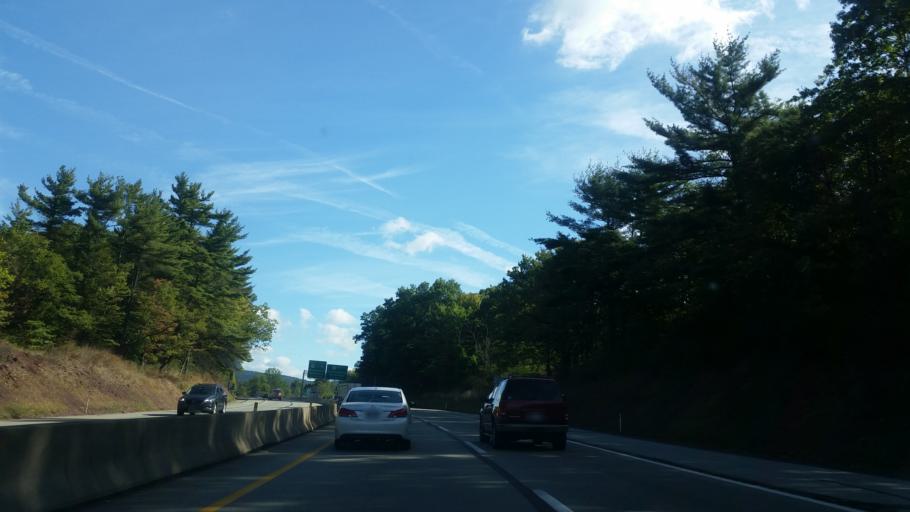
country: US
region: Pennsylvania
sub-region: Bedford County
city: Earlston
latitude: 39.9919
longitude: -78.2372
